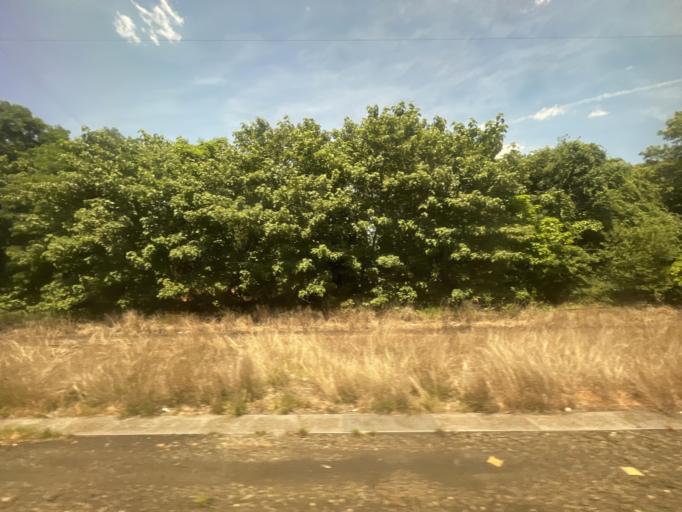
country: US
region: New Jersey
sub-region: Middlesex County
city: New Brunswick
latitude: 40.4836
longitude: -74.4605
